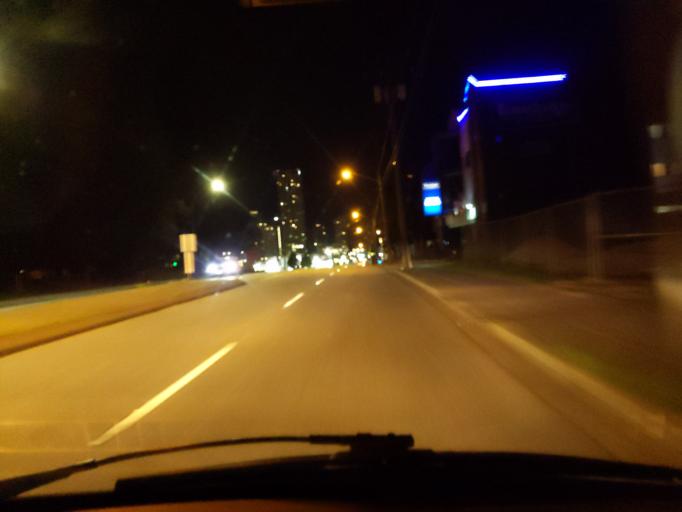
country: CA
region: British Columbia
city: New Westminster
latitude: 49.1916
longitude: -122.8352
